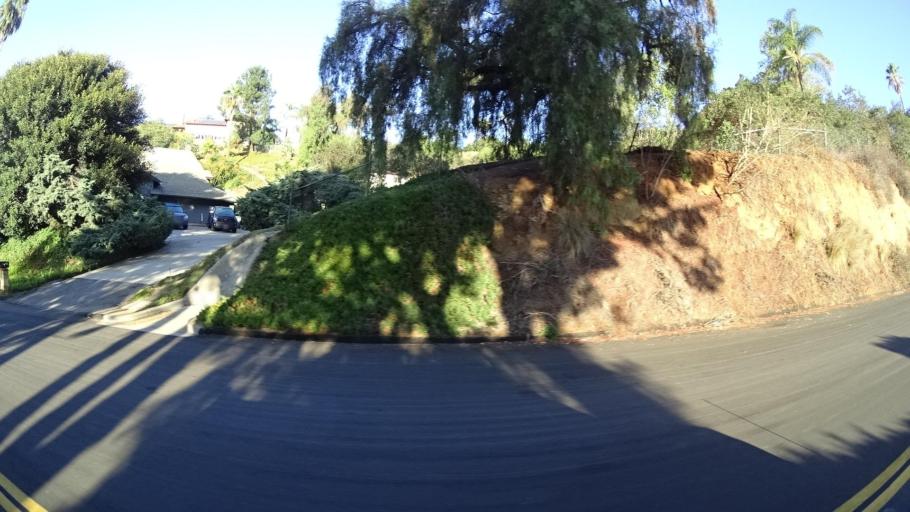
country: US
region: California
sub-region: San Diego County
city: Spring Valley
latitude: 32.7632
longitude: -116.9918
